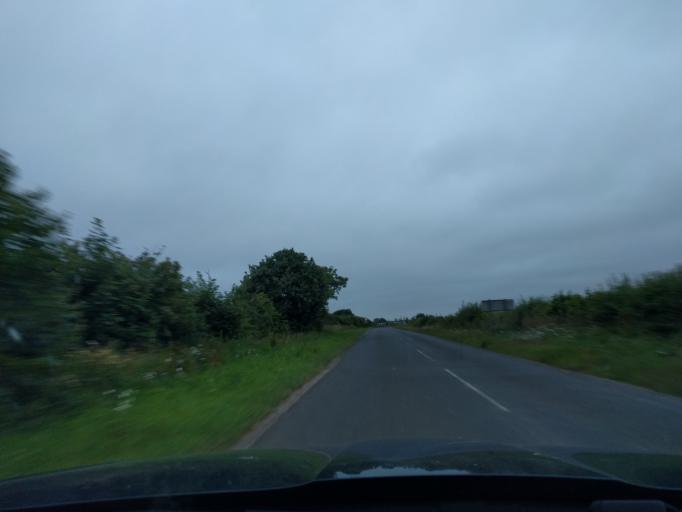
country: GB
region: England
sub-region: Northumberland
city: Acklington
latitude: 55.2690
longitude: -1.6437
